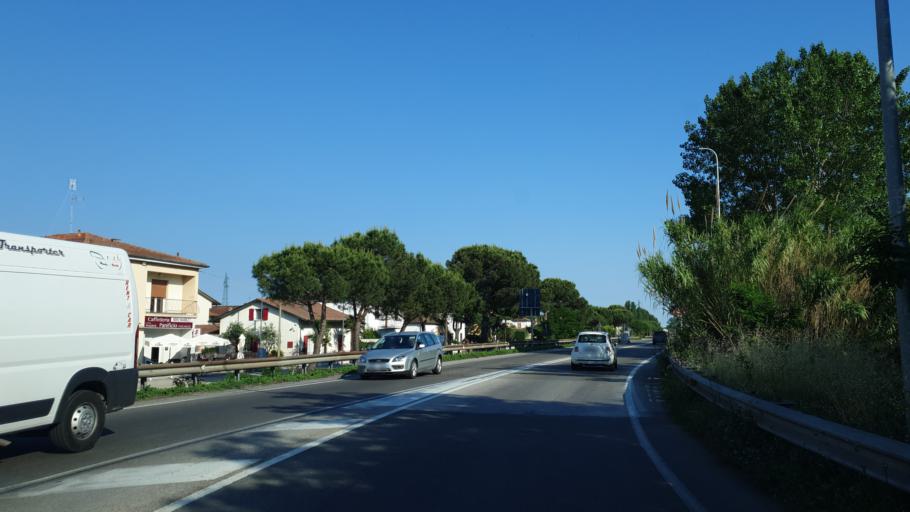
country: IT
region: Emilia-Romagna
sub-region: Provincia di Ravenna
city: Fosso Ghiaia
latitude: 44.3510
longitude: 12.2587
